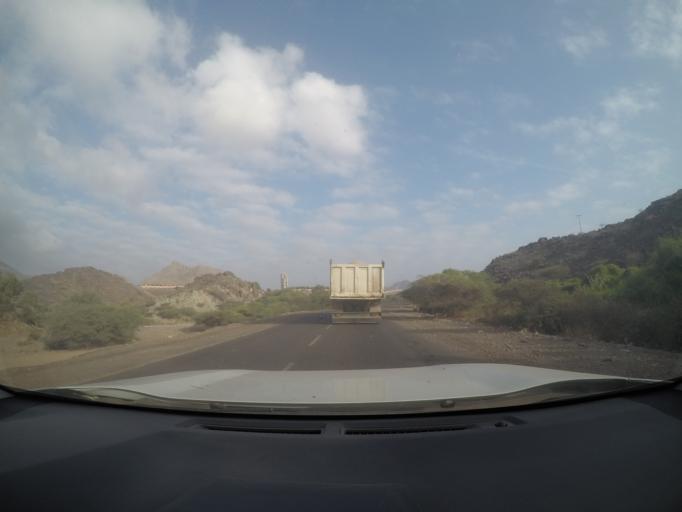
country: YE
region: Lahij
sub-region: Al Milah
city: Al Milah
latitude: 13.3310
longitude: 44.7575
